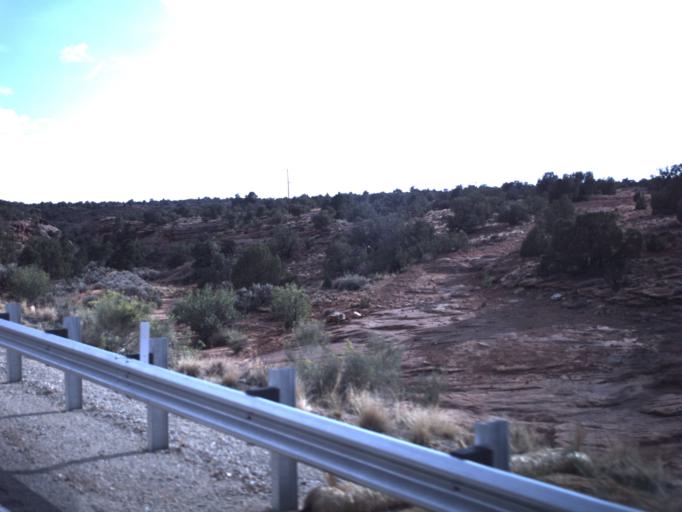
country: US
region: Utah
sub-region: Grand County
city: Moab
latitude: 38.3600
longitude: -109.4348
